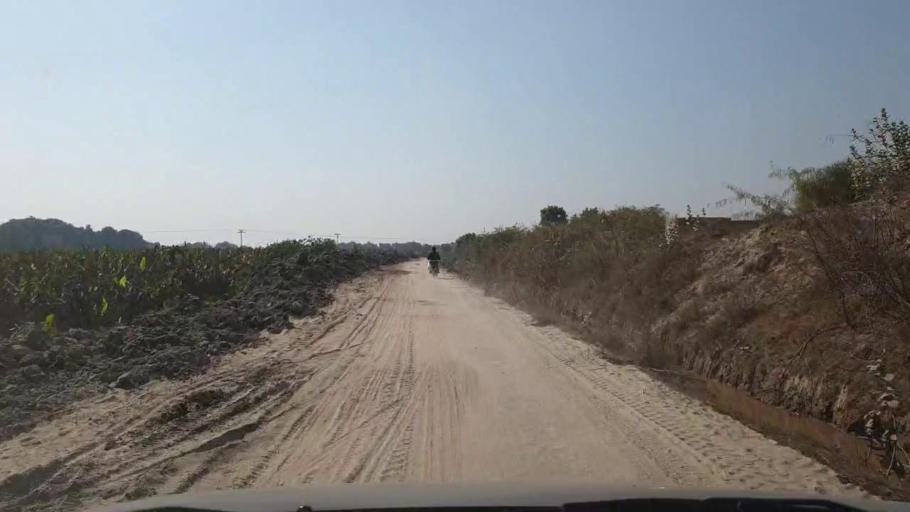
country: PK
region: Sindh
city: Tando Allahyar
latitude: 25.4341
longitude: 68.6416
